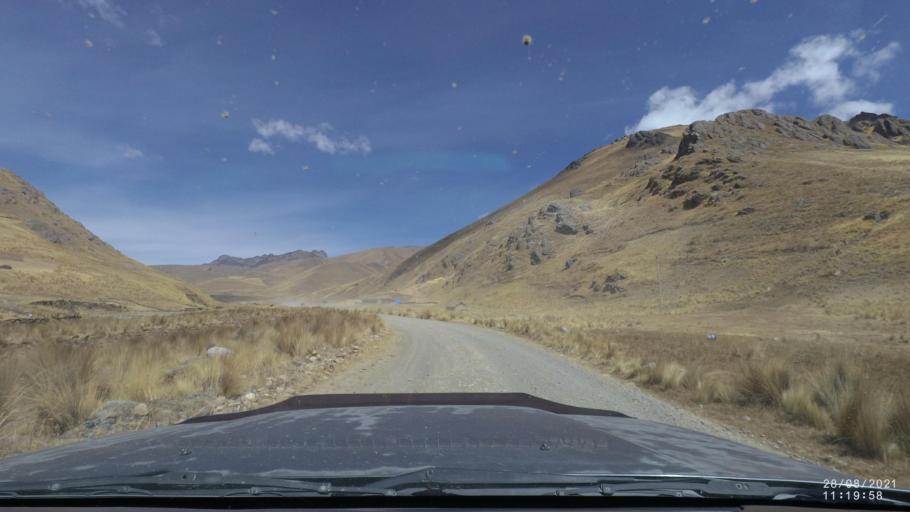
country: BO
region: Cochabamba
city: Cochabamba
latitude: -17.1557
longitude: -66.3371
